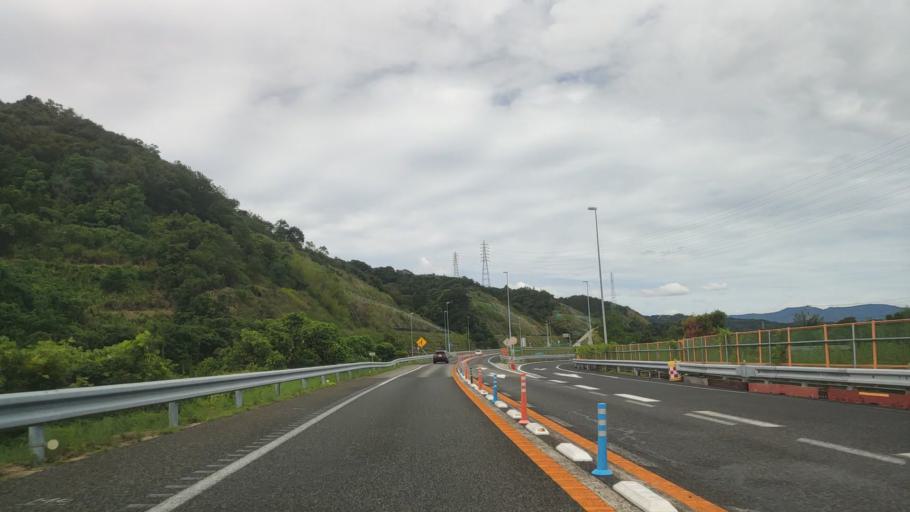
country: JP
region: Wakayama
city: Gobo
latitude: 33.8258
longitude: 135.2198
